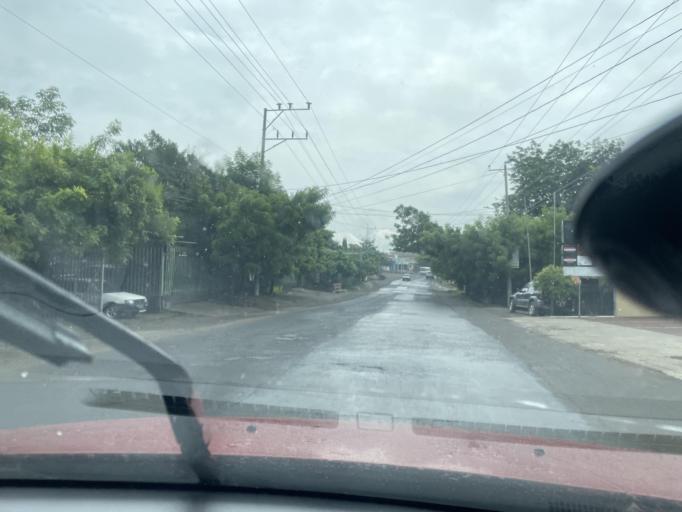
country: SV
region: La Union
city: Santa Rosa de Lima
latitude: 13.6172
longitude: -87.9021
